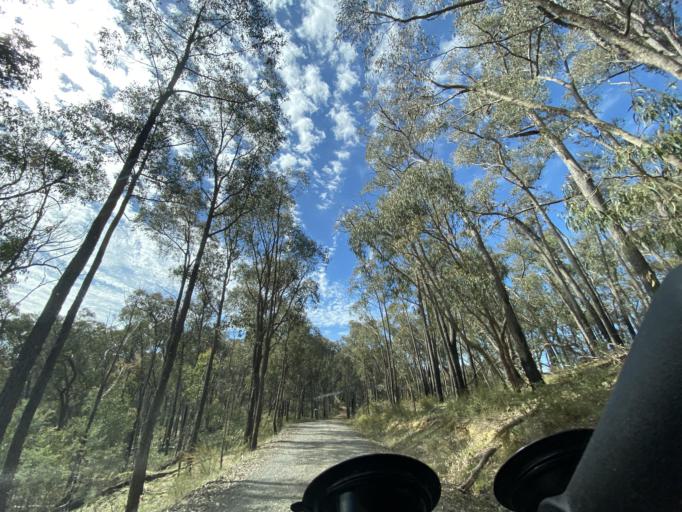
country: AU
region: Victoria
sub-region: Mansfield
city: Mansfield
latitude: -36.8013
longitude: 146.1108
